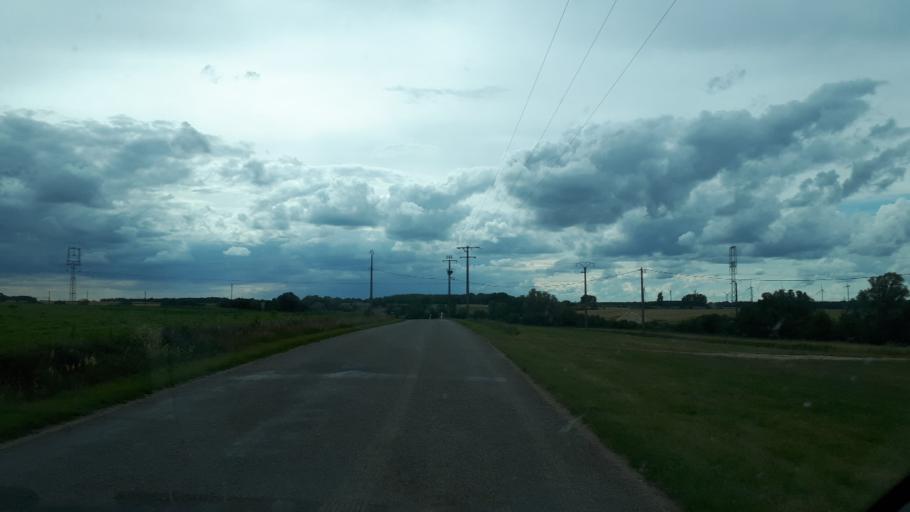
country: FR
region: Centre
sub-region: Departement de l'Indre
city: Reuilly
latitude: 47.0945
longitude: 2.0013
